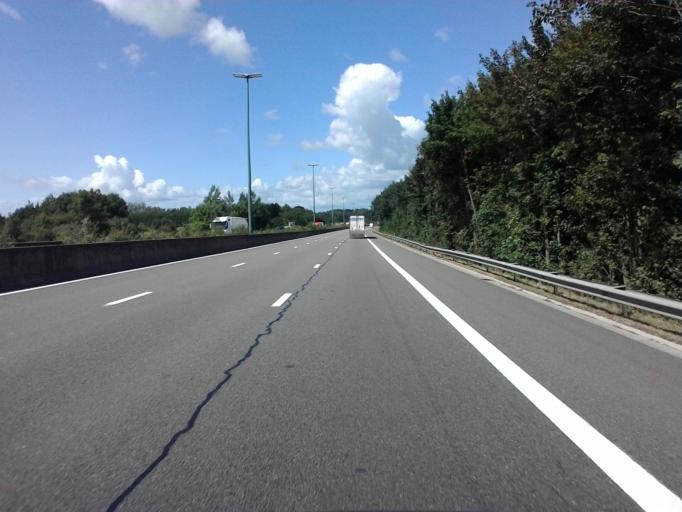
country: BE
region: Wallonia
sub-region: Province du Luxembourg
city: Habay-la-Vieille
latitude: 49.6959
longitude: 5.6786
